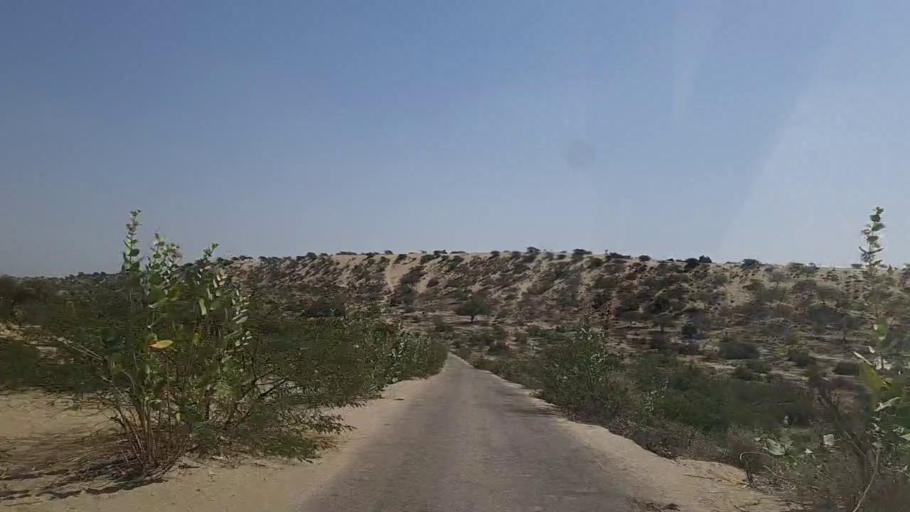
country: PK
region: Sindh
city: Diplo
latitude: 24.4845
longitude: 69.4508
